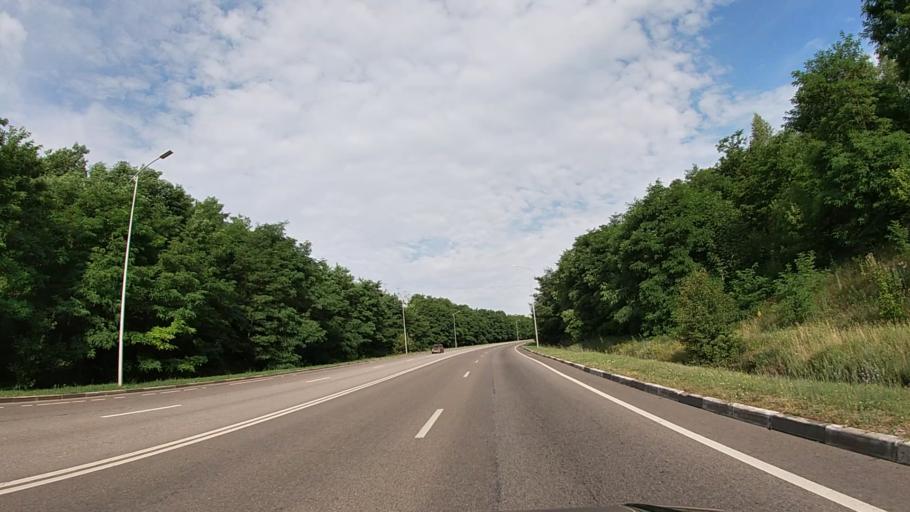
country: RU
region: Belgorod
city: Severnyy
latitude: 50.6358
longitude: 36.4542
